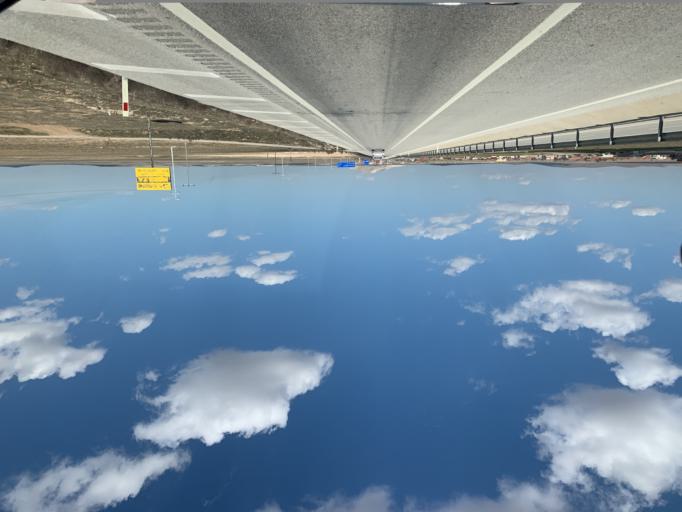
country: TR
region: Konya
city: Cihanbeyli
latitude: 38.5058
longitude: 32.8501
